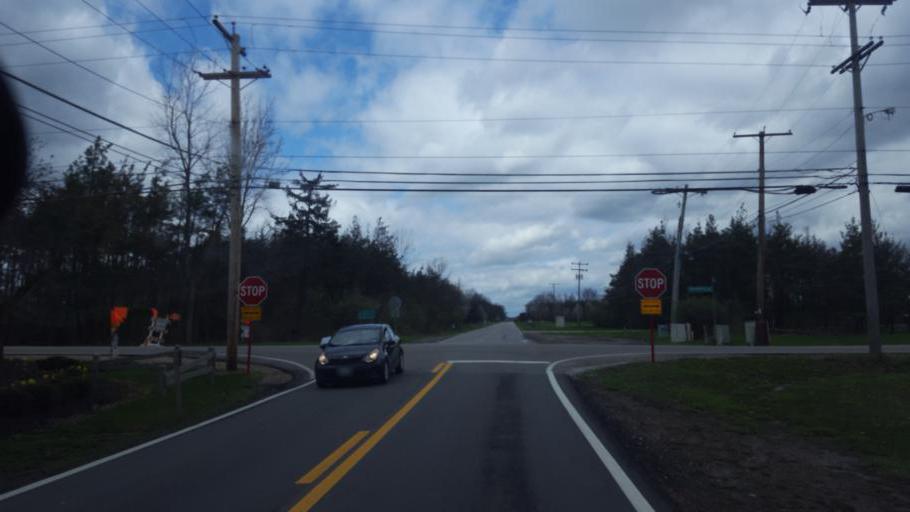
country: US
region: Ohio
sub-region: Franklin County
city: New Albany
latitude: 40.1297
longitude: -82.8582
